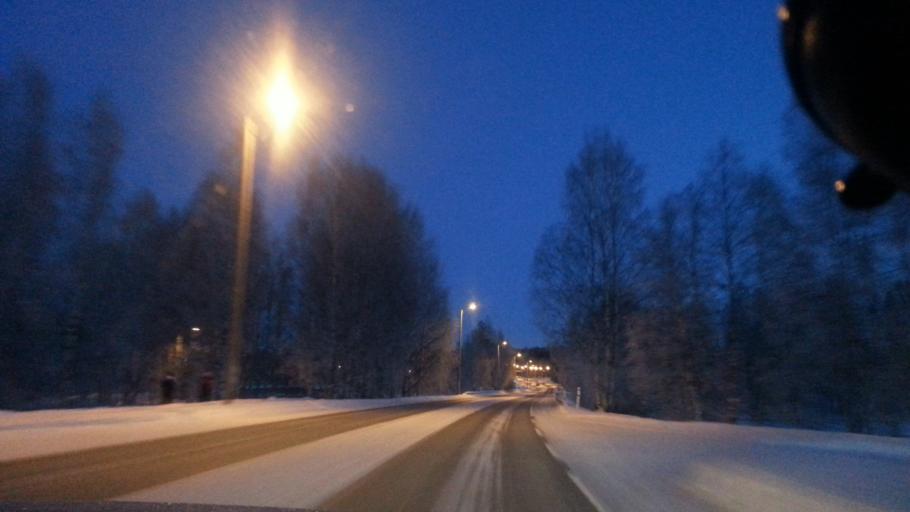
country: FI
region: Lapland
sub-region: Rovaniemi
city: Rovaniemi
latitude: 66.4862
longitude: 25.7510
